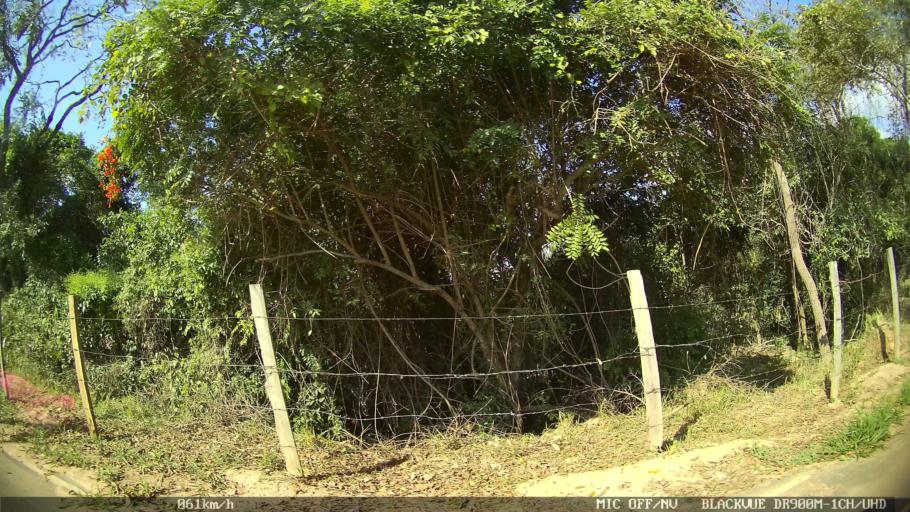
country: BR
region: Sao Paulo
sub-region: Indaiatuba
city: Indaiatuba
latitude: -22.9955
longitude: -47.1977
